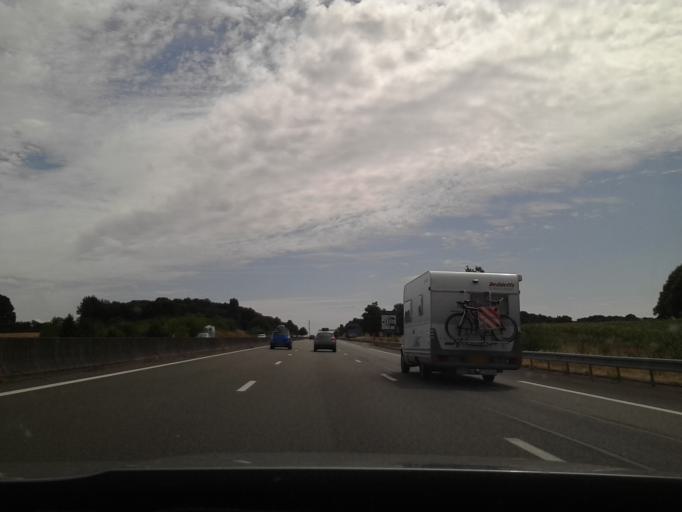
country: FR
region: Pays de la Loire
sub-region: Departement de la Sarthe
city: Sarge-les-le-Mans
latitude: 48.0585
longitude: 0.2320
